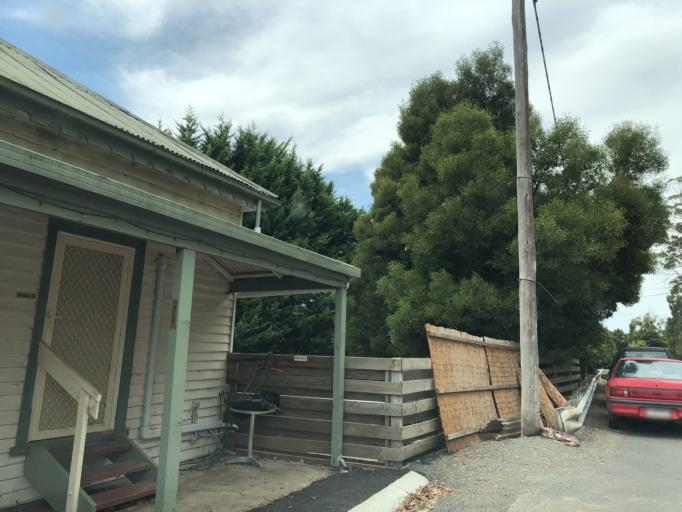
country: AU
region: Victoria
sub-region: Moorabool
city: Bacchus Marsh
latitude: -37.4704
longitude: 144.3076
